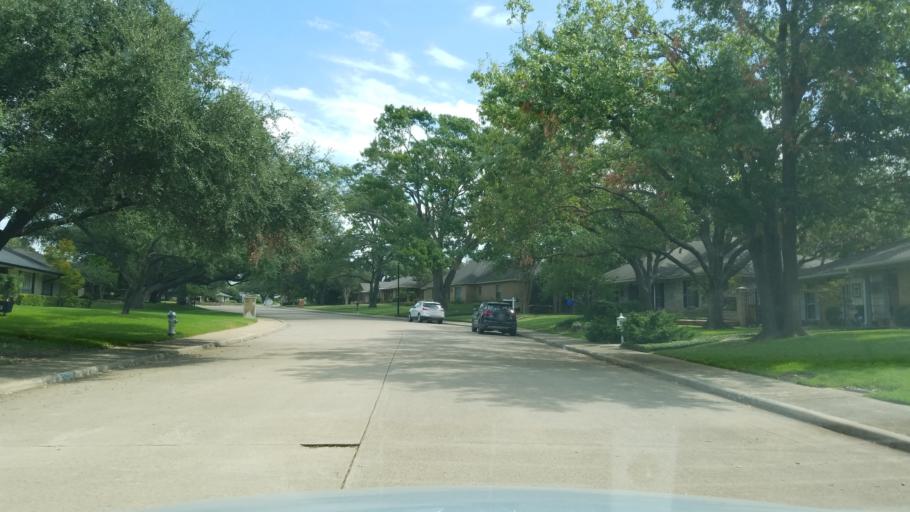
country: US
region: Texas
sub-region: Dallas County
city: Addison
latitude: 32.9567
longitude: -96.7900
